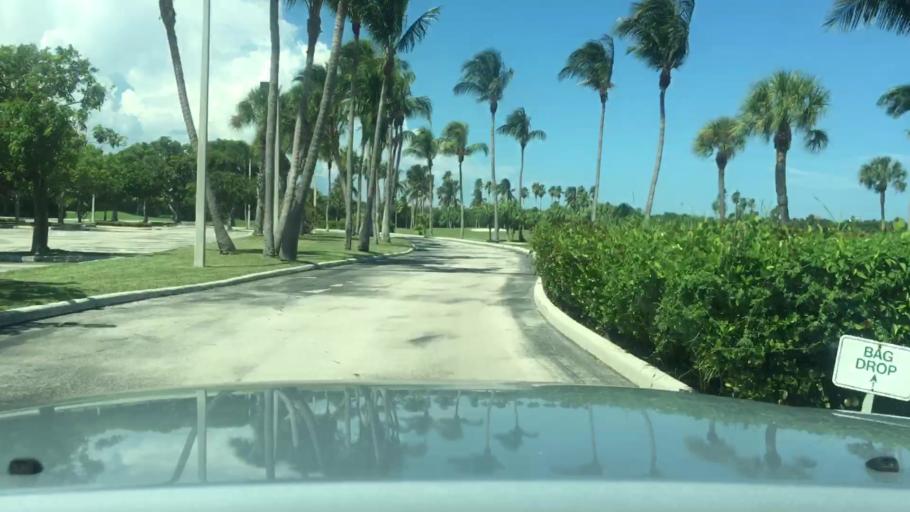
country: US
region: Florida
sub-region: Miami-Dade County
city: Key Biscayne
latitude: 25.7159
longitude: -80.1581
